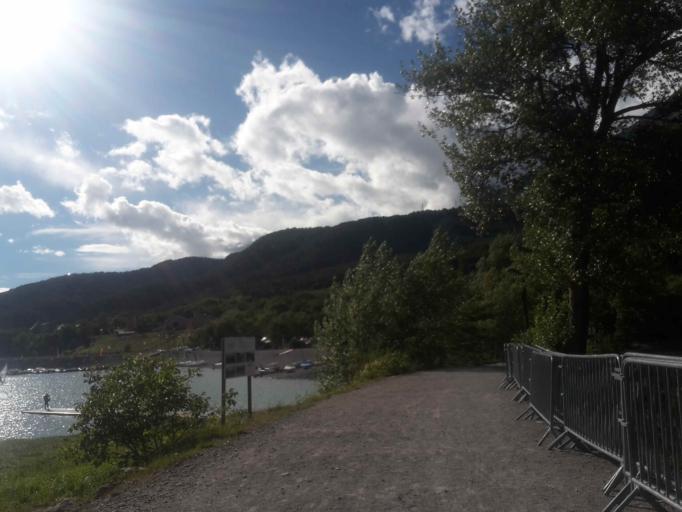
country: FR
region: Provence-Alpes-Cote d'Azur
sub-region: Departement des Hautes-Alpes
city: Embrun
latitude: 44.5467
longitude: 6.4678
